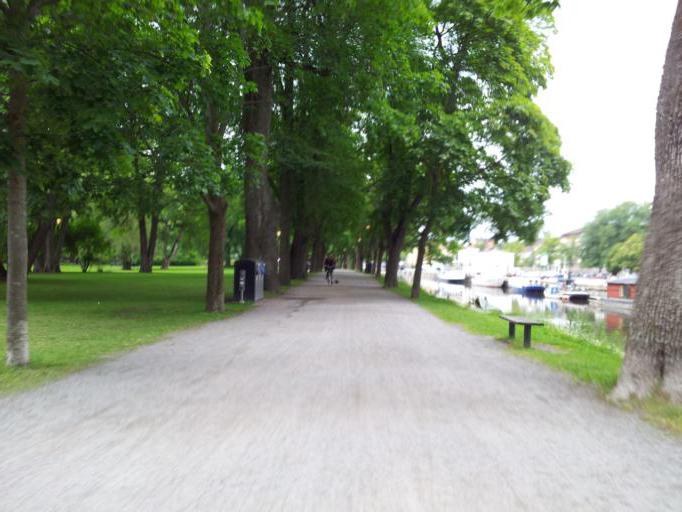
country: SE
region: Uppsala
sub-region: Uppsala Kommun
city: Uppsala
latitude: 59.8515
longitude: 17.6452
